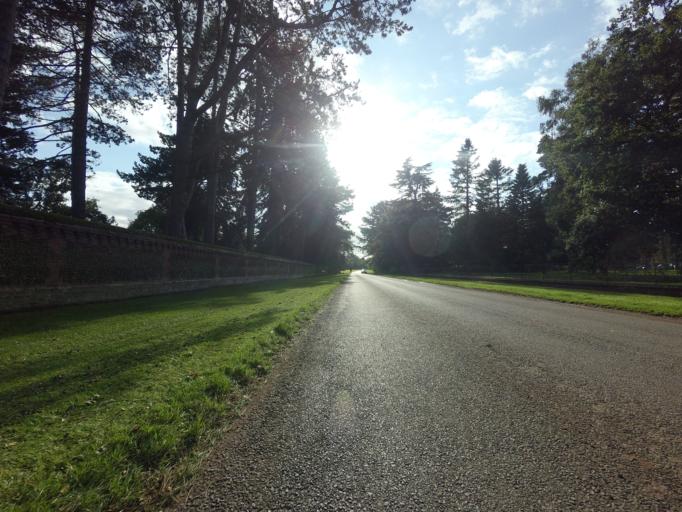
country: GB
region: England
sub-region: Norfolk
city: Dersingham
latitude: 52.8312
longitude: 0.5098
